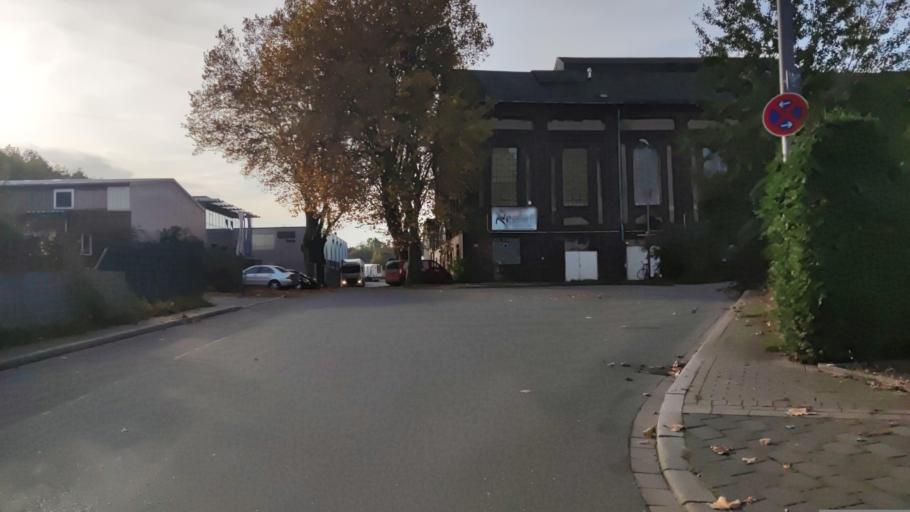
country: DE
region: North Rhine-Westphalia
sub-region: Regierungsbezirk Arnsberg
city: Herne
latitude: 51.5177
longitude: 7.2192
